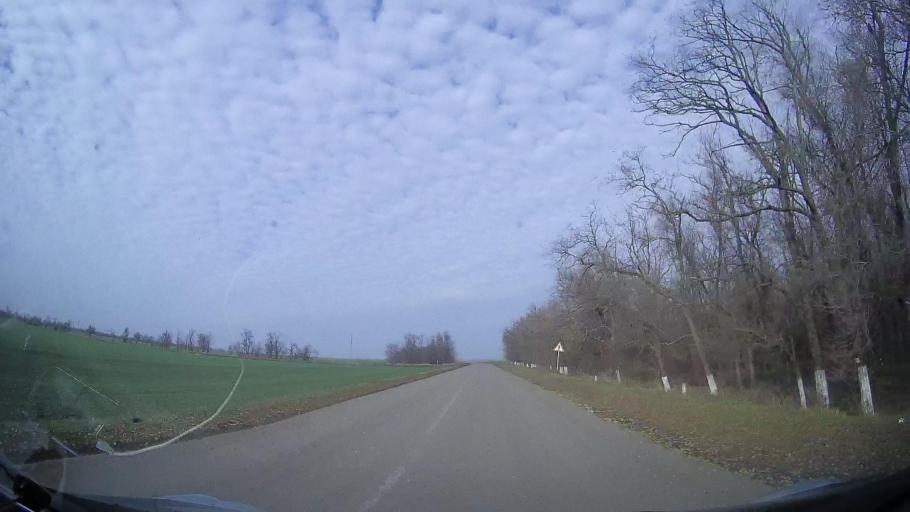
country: RU
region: Rostov
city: Gigant
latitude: 46.9273
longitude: 41.2462
